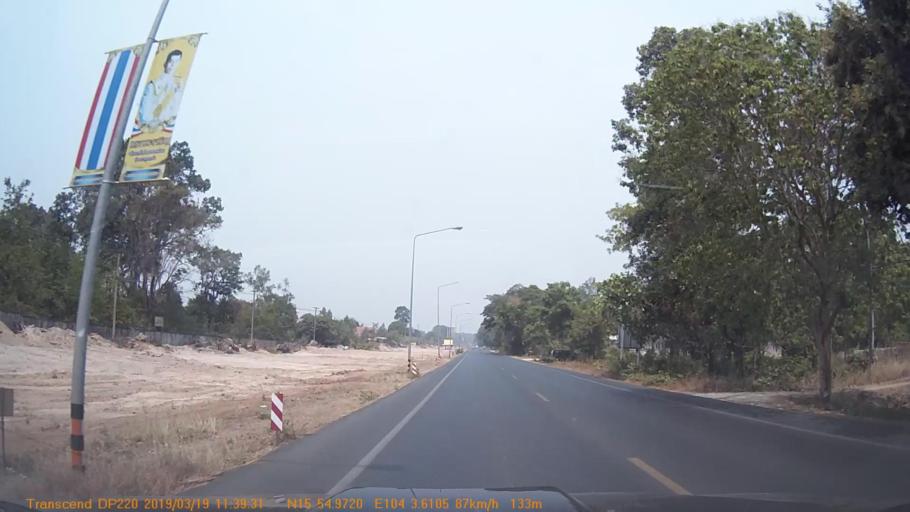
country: TH
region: Yasothon
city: Yasothon
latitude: 15.9163
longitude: 104.0601
